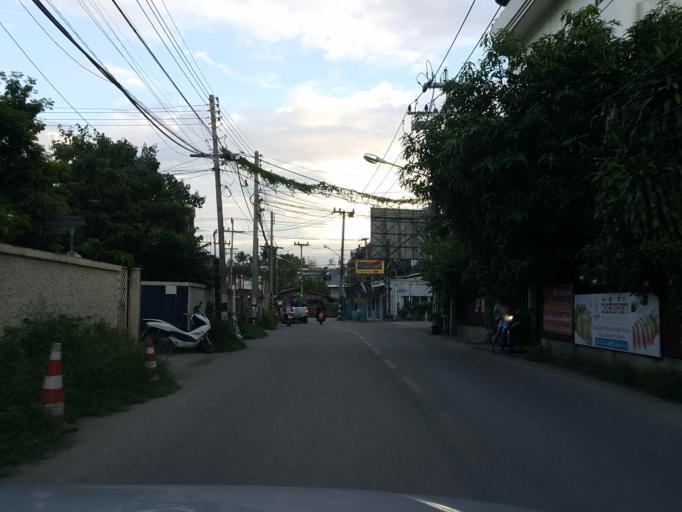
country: TH
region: Chiang Mai
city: Chiang Mai
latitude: 18.7947
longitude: 99.0009
